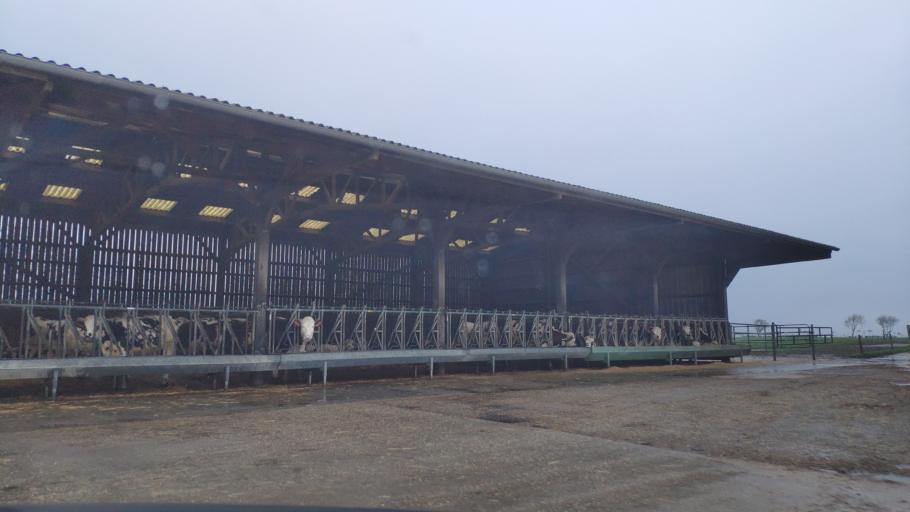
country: FR
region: Haute-Normandie
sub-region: Departement de la Seine-Maritime
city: Neville
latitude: 49.7729
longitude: 0.7156
